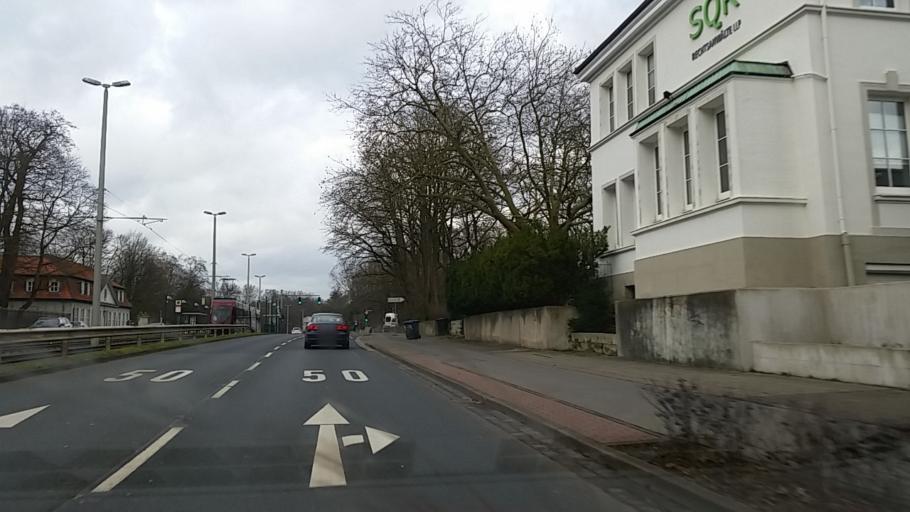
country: DE
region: Lower Saxony
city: Braunschweig
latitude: 52.2397
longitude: 10.5279
